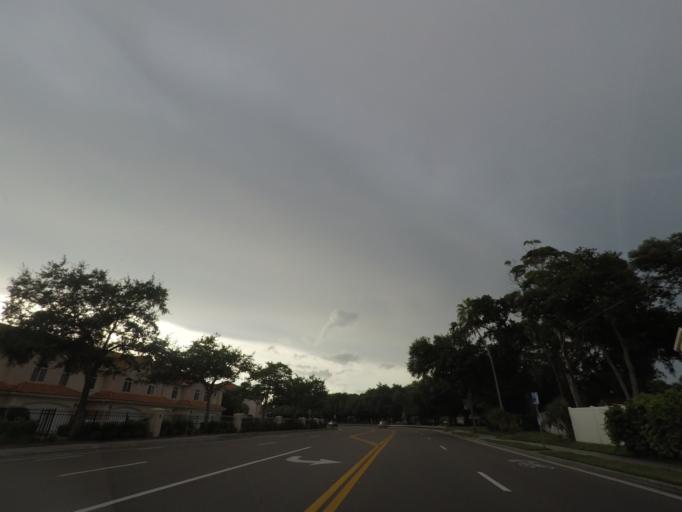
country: US
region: Florida
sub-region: Pinellas County
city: South Pasadena
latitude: 27.7565
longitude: -82.7227
